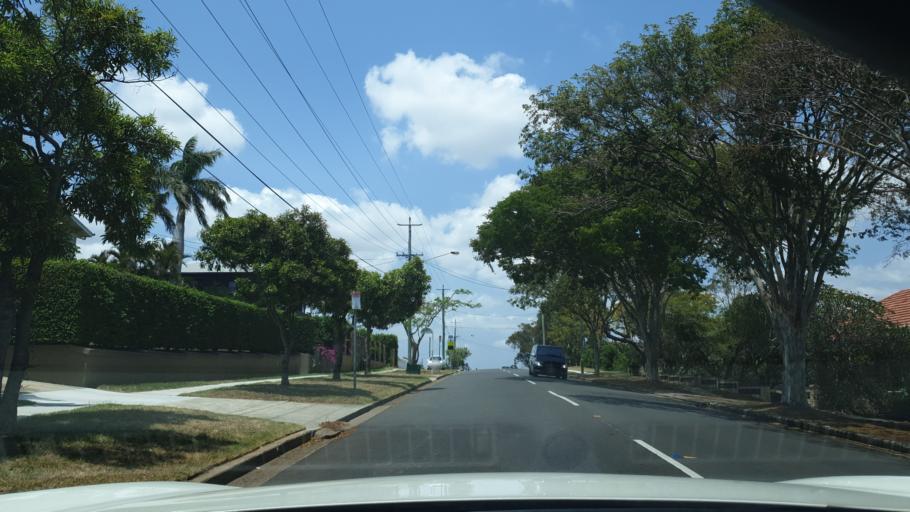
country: AU
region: Queensland
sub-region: Brisbane
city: Chermside West
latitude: -27.3665
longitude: 153.0262
